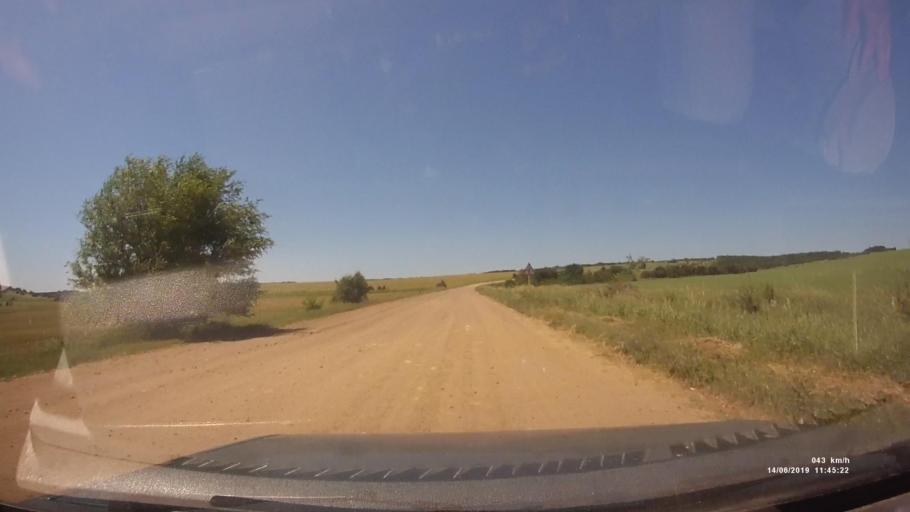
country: RU
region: Rostov
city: Kazanskaya
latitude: 49.8518
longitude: 41.3152
